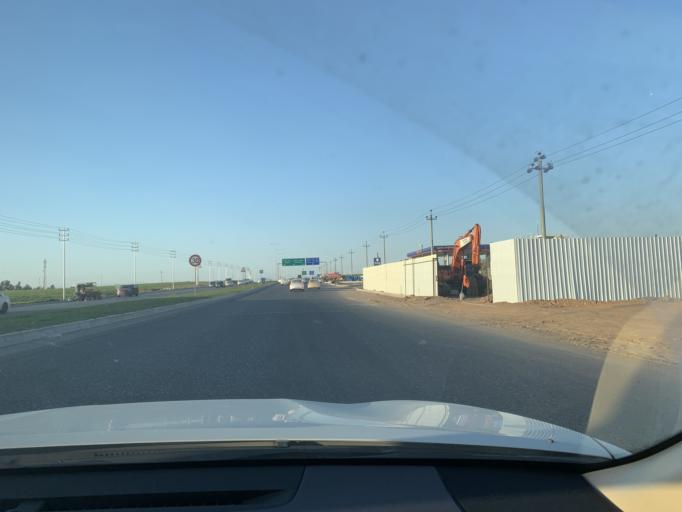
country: IQ
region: Arbil
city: Erbil
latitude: 36.2824
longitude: 44.0160
